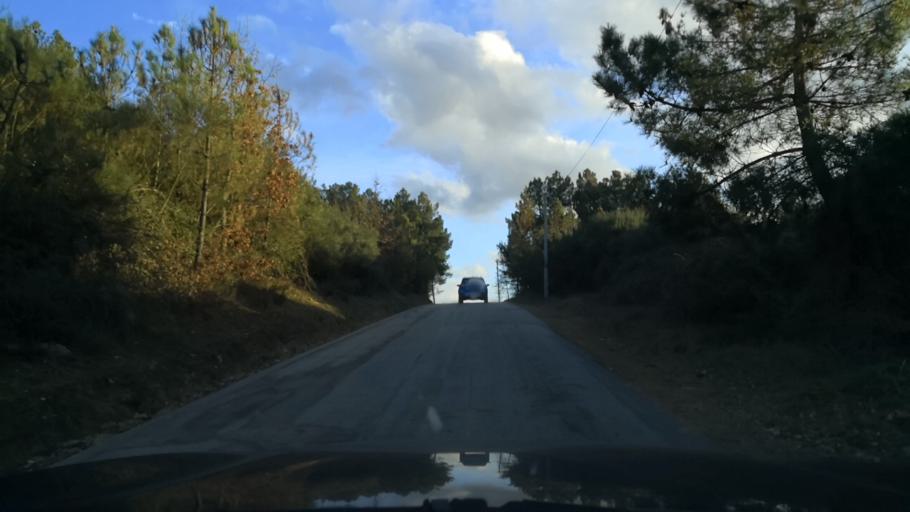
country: PT
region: Braganca
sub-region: Carrazeda de Ansiaes
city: Carrazeda de Anciaes
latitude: 41.2276
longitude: -7.3385
